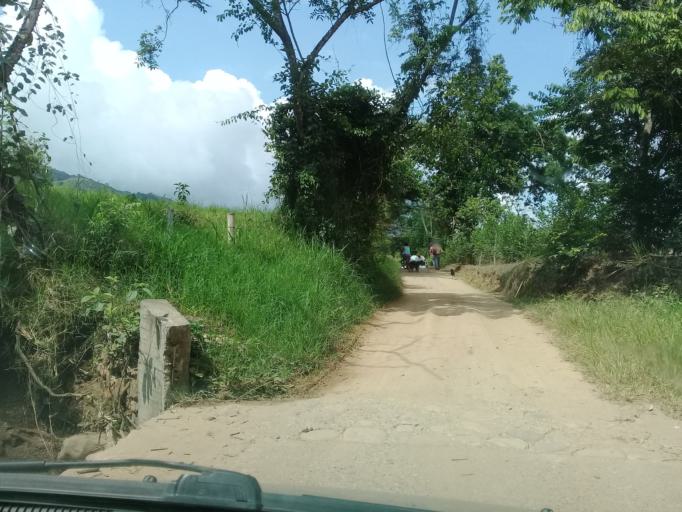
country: CO
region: Cundinamarca
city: Guaduas
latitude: 5.0238
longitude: -74.6088
